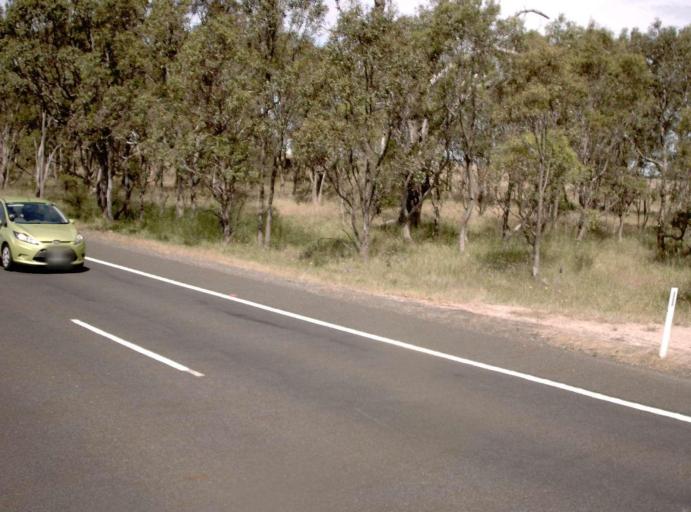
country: AU
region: Victoria
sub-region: East Gippsland
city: Bairnsdale
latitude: -37.8898
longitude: 147.3881
